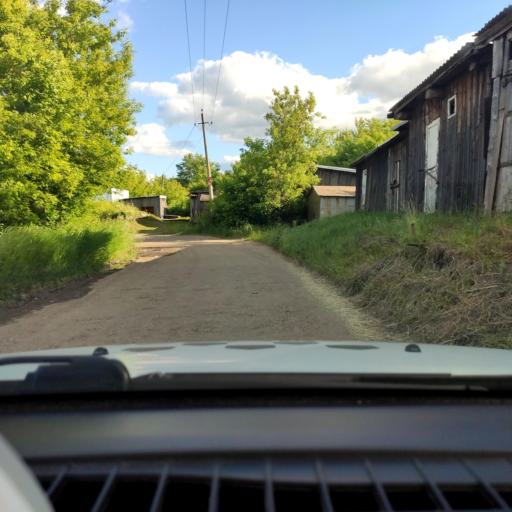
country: RU
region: Perm
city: Ferma
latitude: 57.9057
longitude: 56.2989
